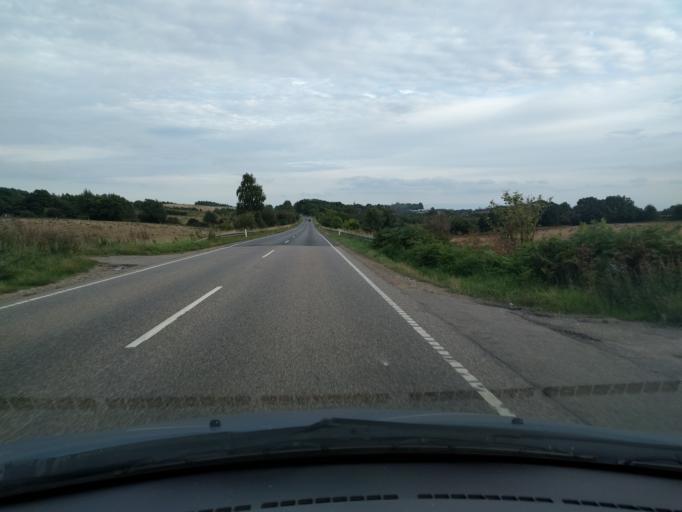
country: DK
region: Zealand
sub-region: Vordingborg Kommune
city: Nyrad
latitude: 55.0072
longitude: 11.9788
